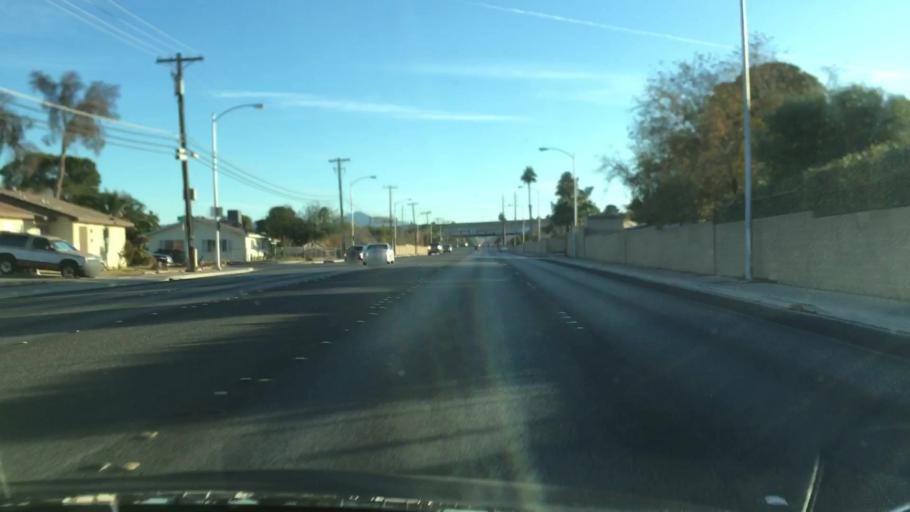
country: US
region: Nevada
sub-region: Clark County
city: Whitney
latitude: 36.0962
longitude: -115.0733
